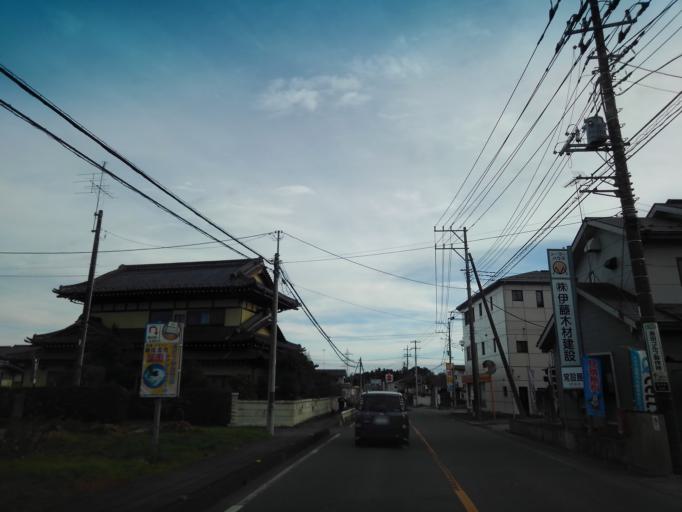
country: JP
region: Saitama
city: Morohongo
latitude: 35.9145
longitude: 139.3268
